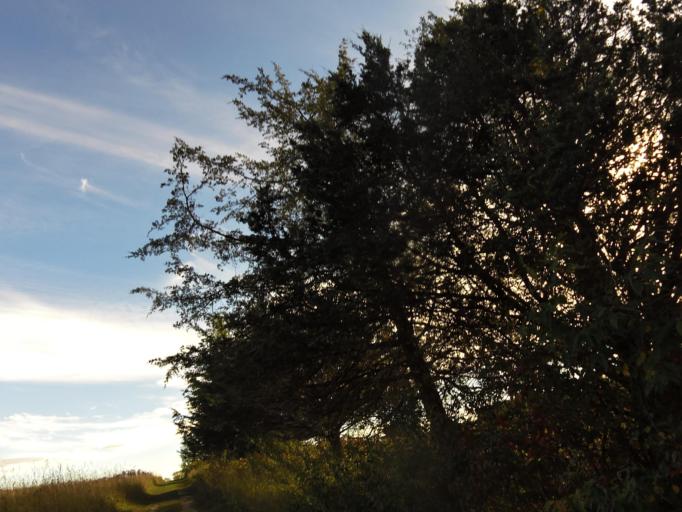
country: US
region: Minnesota
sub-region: Washington County
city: Afton
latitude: 44.8697
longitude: -92.7916
